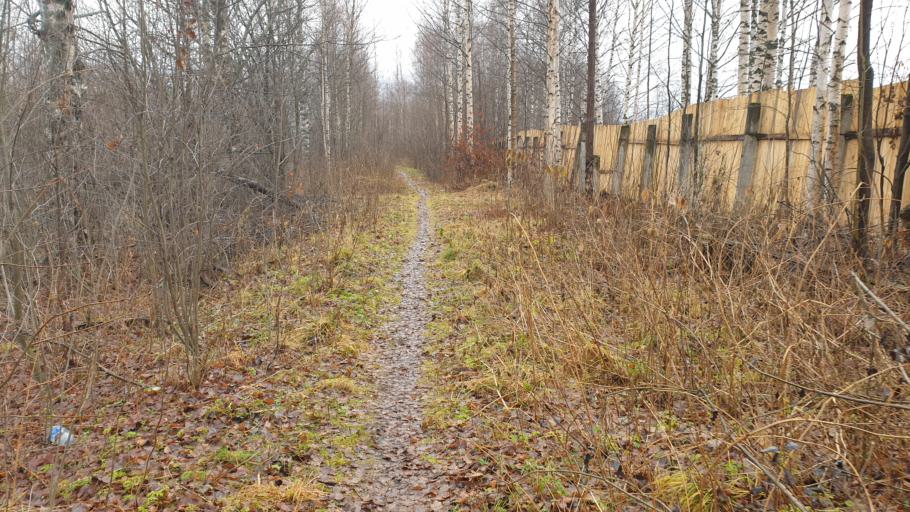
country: RU
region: Kirov
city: Kirs
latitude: 59.3343
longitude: 52.2391
